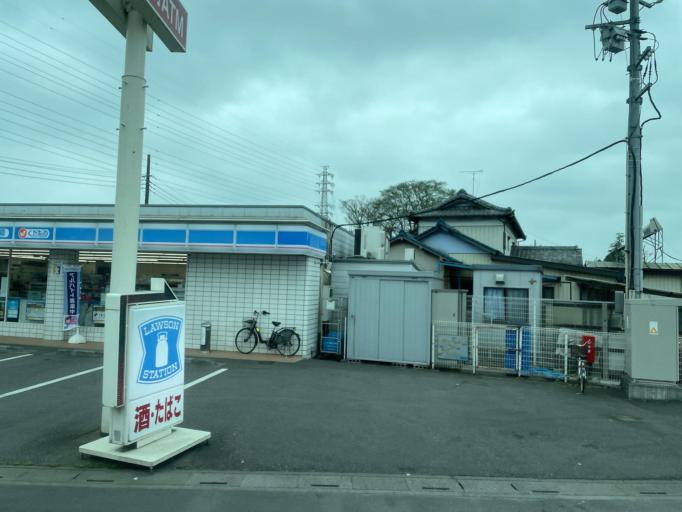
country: JP
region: Saitama
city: Iwatsuki
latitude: 35.9215
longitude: 139.7175
